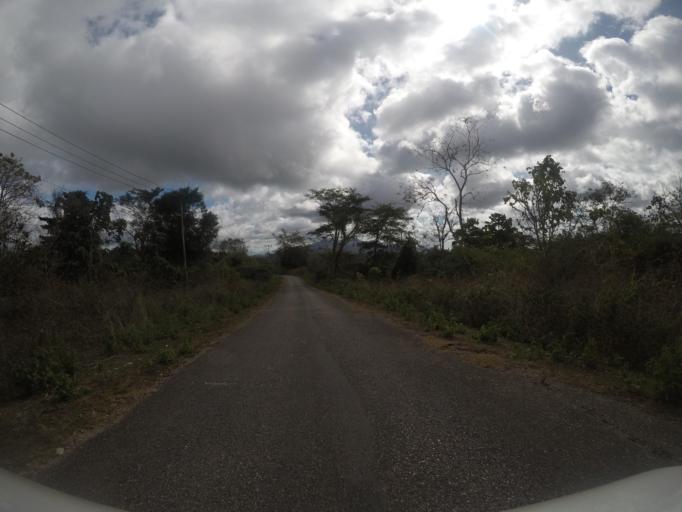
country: TL
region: Lautem
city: Lospalos
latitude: -8.5375
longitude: 126.9089
